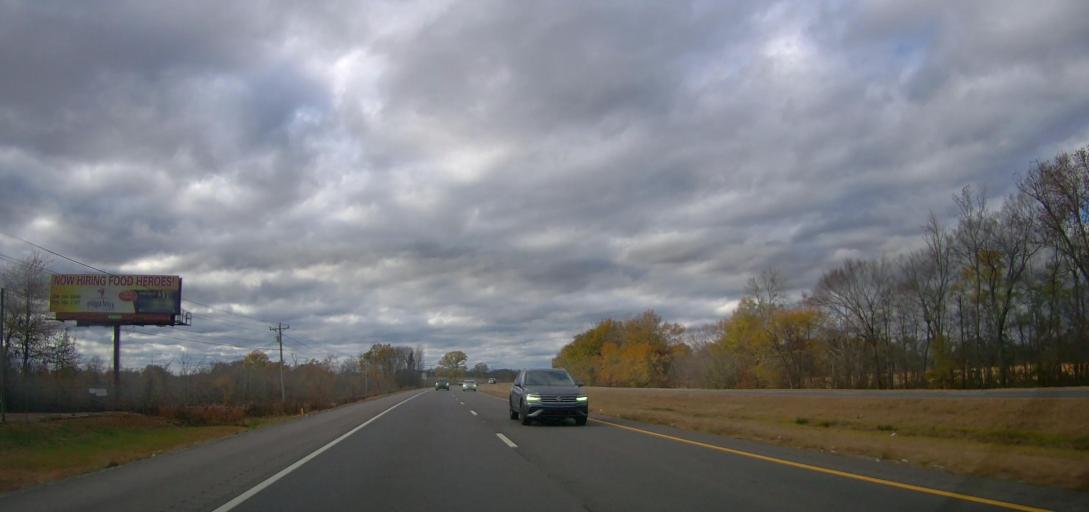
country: US
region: Alabama
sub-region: Lawrence County
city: Moulton
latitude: 34.4658
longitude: -87.2589
